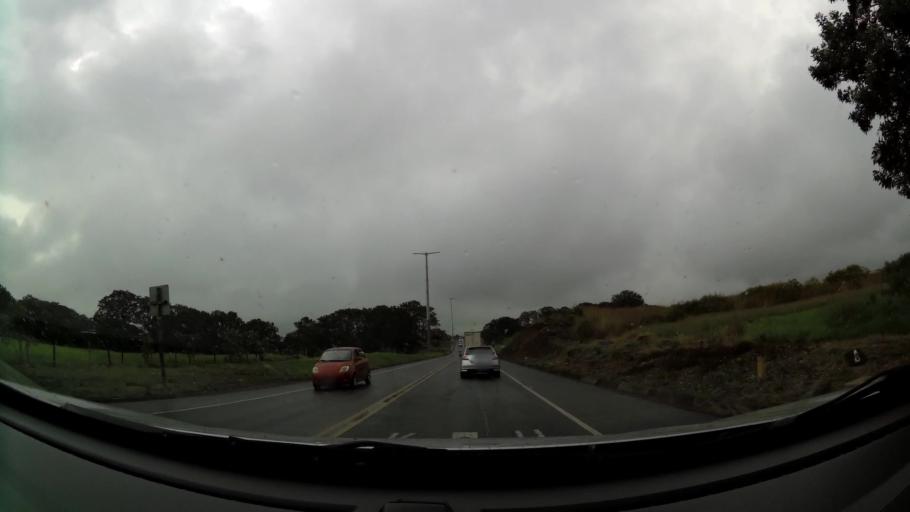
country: CR
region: Alajuela
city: Carrillos
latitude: 9.9870
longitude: -84.2697
